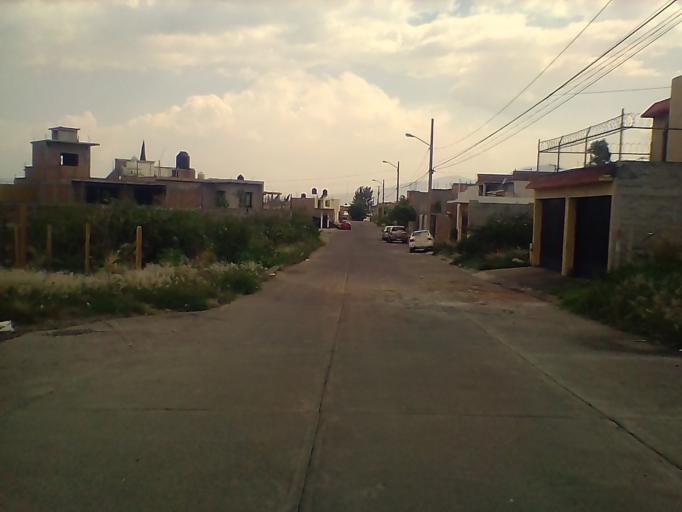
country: MX
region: Michoacan
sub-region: Morelia
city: San Antonio
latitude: 19.7128
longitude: -101.2398
